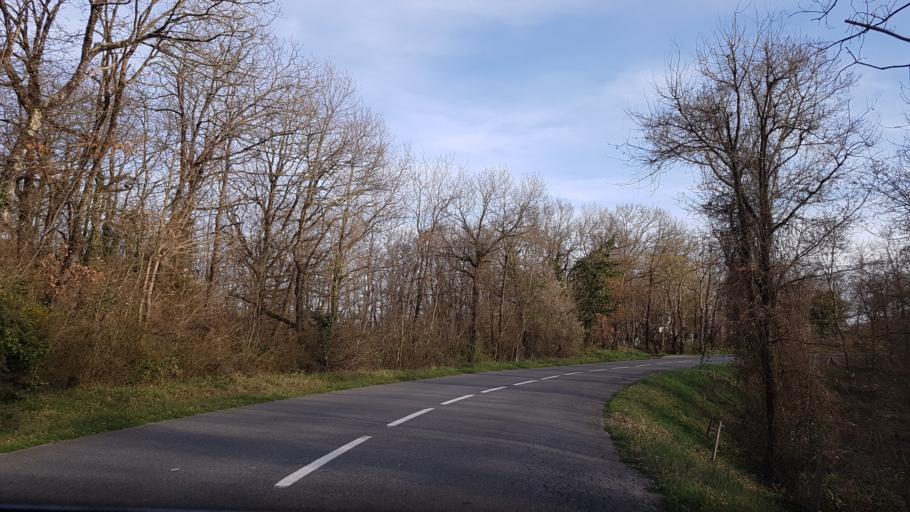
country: FR
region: Languedoc-Roussillon
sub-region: Departement de l'Aude
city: Villeneuve-la-Comptal
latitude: 43.2356
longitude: 1.9207
